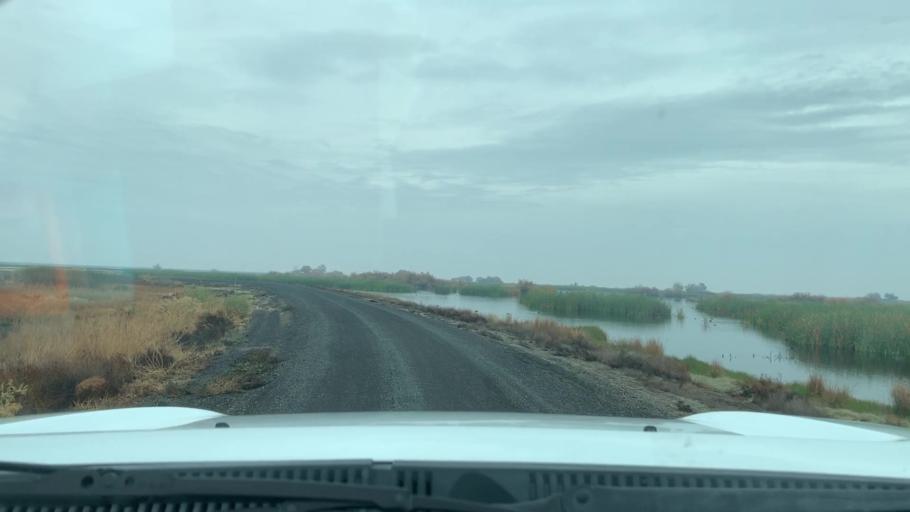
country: US
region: California
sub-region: Kern County
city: Lost Hills
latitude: 35.7479
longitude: -119.5943
